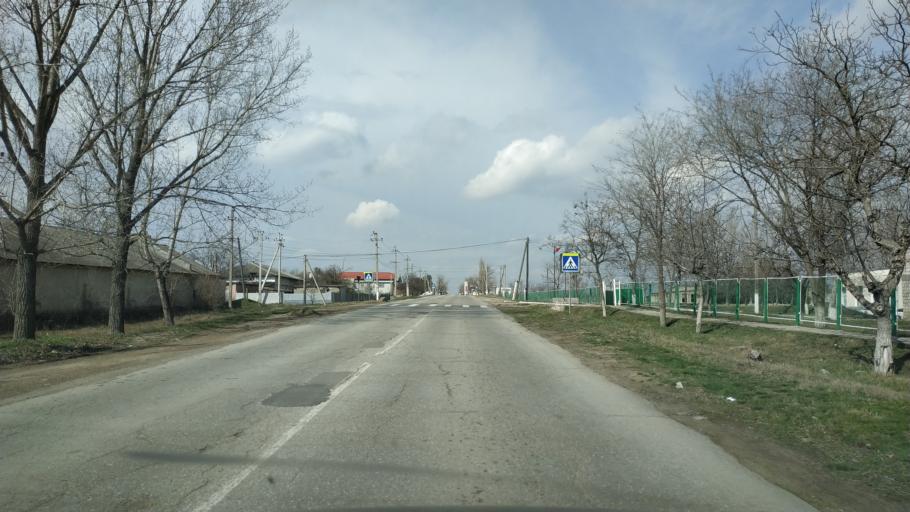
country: MD
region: Gagauzia
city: Vulcanesti
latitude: 45.6953
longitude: 28.4043
